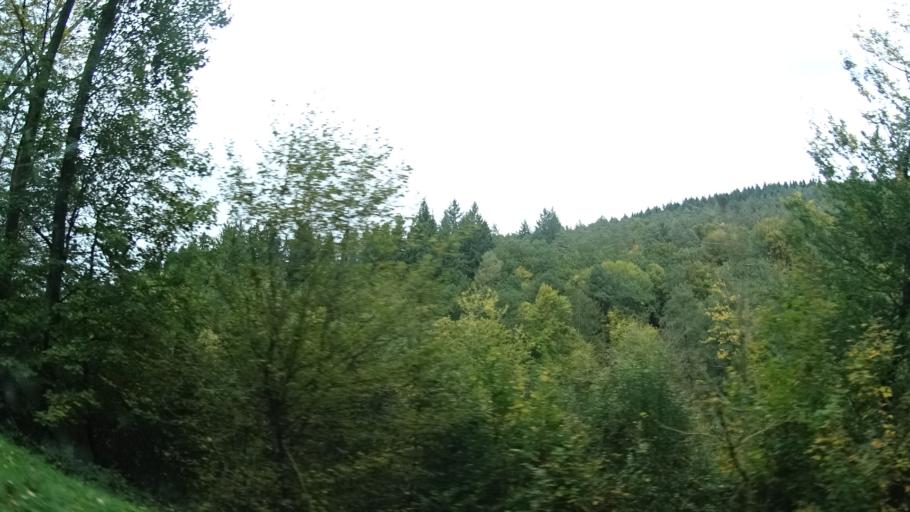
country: DE
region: Bavaria
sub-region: Regierungsbezirk Unterfranken
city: Kirchzell
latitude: 49.5647
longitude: 9.1392
